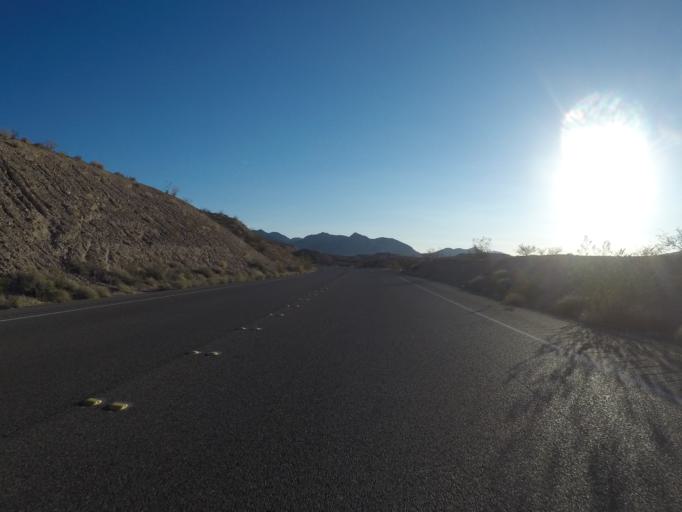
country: US
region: Nevada
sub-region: Clark County
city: Moapa Valley
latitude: 36.2997
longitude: -114.4902
